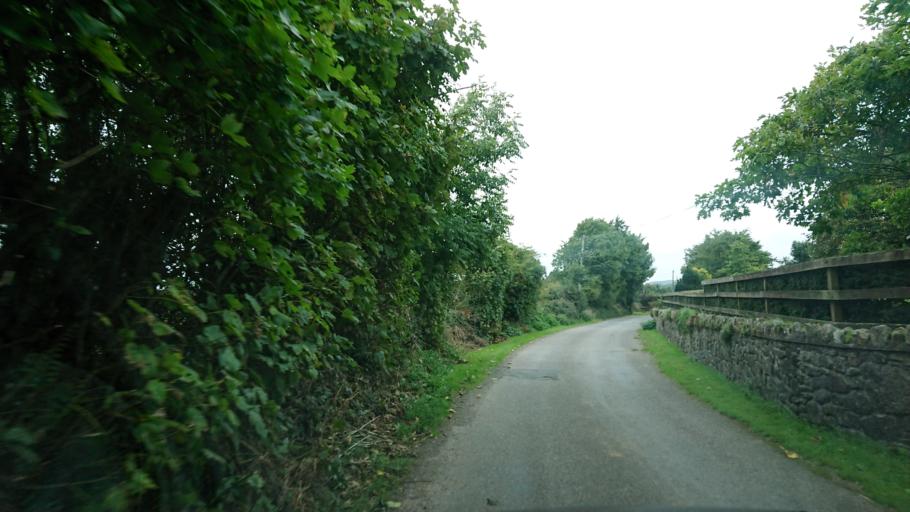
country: IE
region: Munster
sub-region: Waterford
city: Waterford
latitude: 52.2148
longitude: -7.0427
